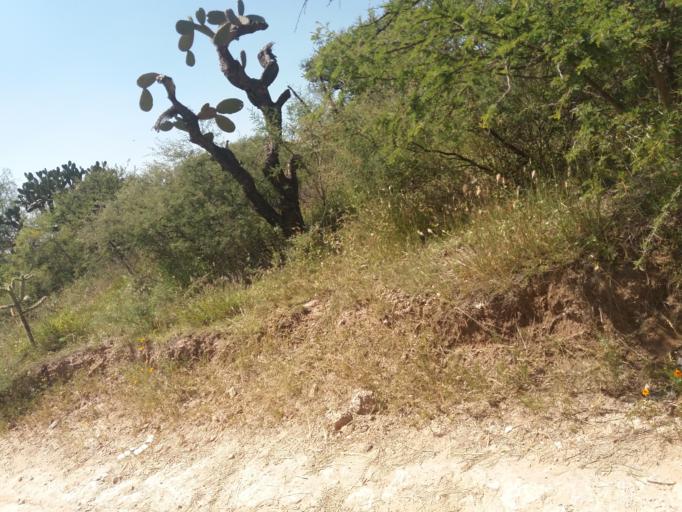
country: MX
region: Aguascalientes
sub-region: Aguascalientes
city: Penuelas (El Cienegal)
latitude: 21.7694
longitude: -102.2394
